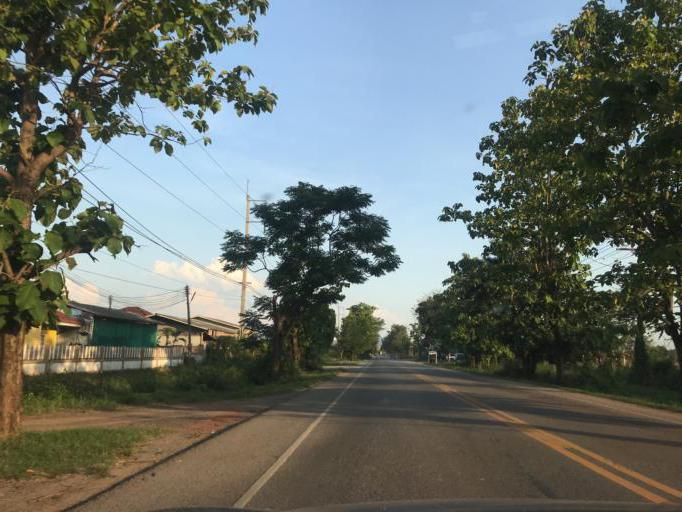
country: TH
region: Phayao
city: Chiang Kham
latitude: 19.5297
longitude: 100.2932
